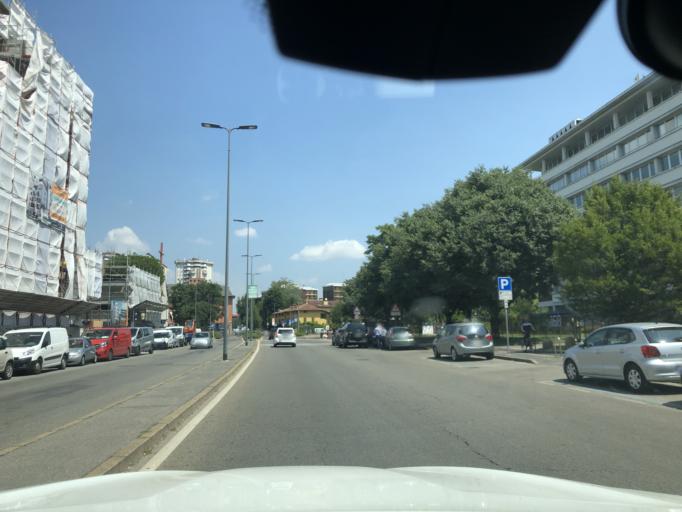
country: IT
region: Lombardy
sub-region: Citta metropolitana di Milano
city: Milano
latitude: 45.4960
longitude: 9.2078
